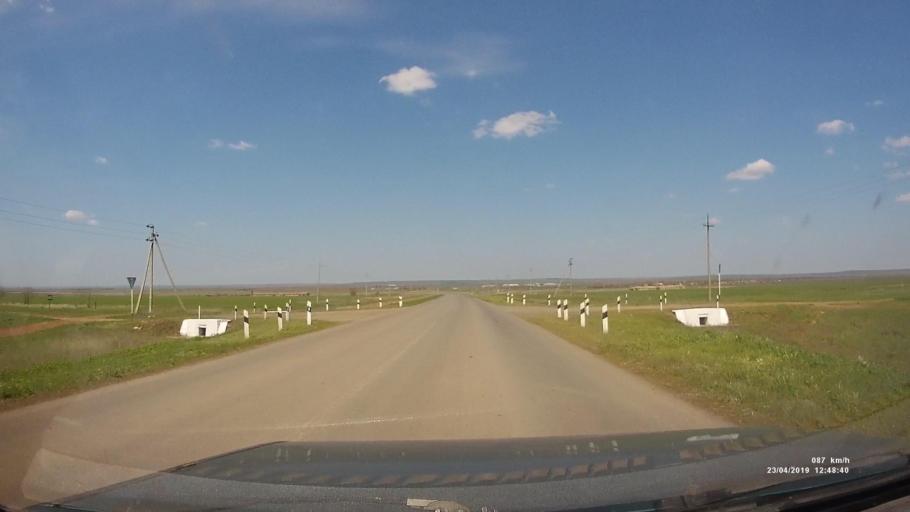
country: RU
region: Kalmykiya
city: Yashalta
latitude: 46.5274
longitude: 42.6389
